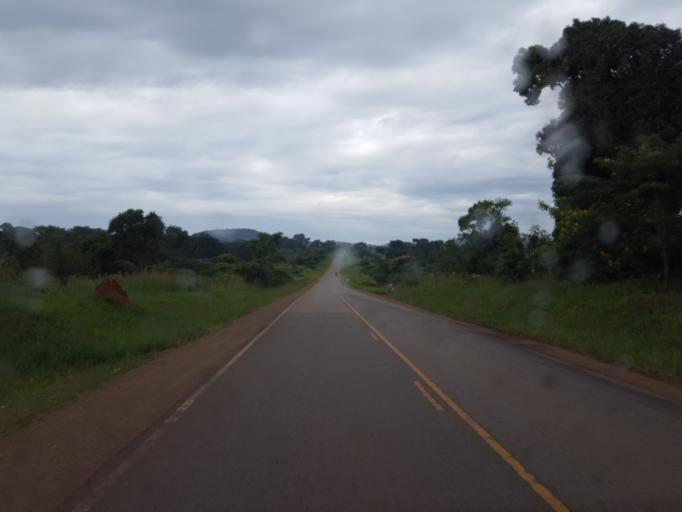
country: UG
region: Central Region
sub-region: Kiboga District
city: Kiboga
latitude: 0.9984
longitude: 31.7006
